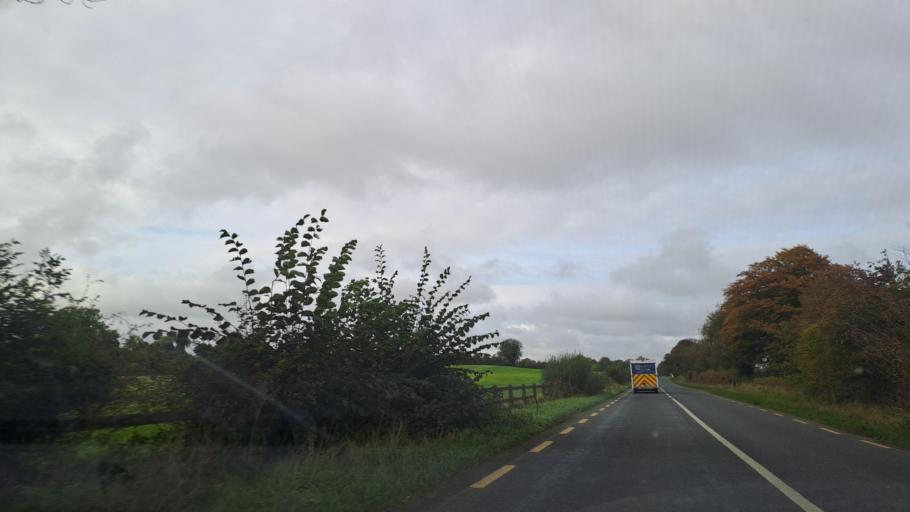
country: IE
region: Leinster
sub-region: An Mhi
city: Navan
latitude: 53.7604
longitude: -6.7249
